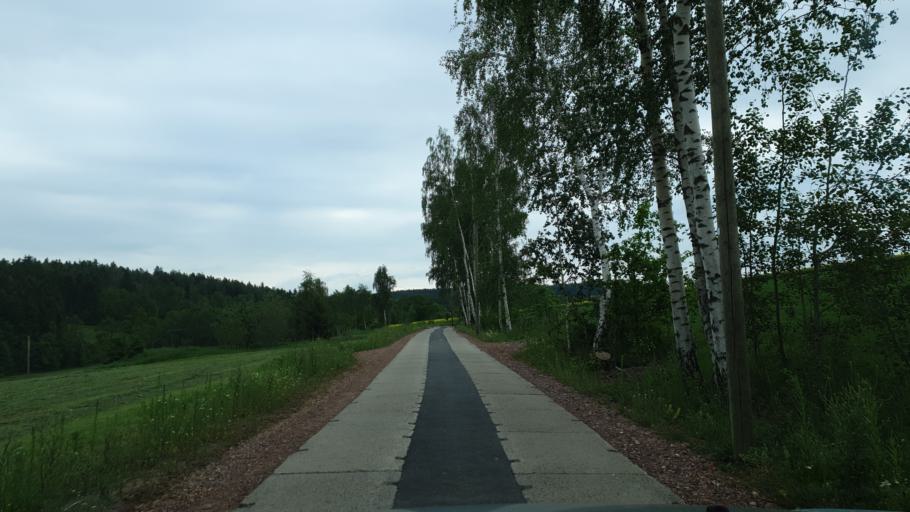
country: DE
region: Saxony
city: Stollberg
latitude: 50.6934
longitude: 12.7803
